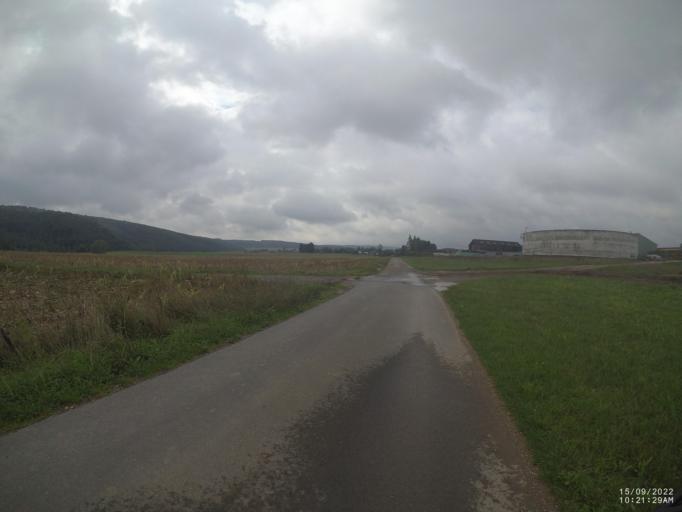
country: DE
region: Rheinland-Pfalz
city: Nohn
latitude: 50.3384
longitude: 6.7891
